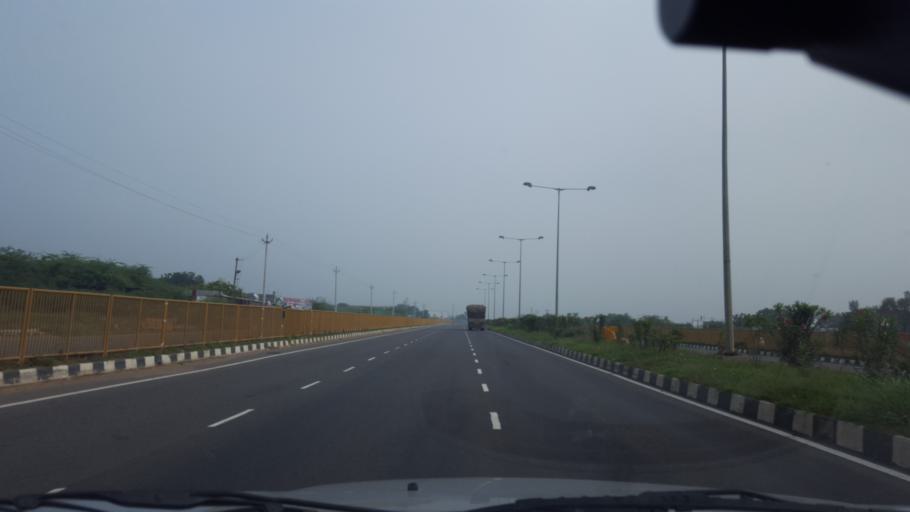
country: IN
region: Andhra Pradesh
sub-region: Guntur
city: Chilakalurupet
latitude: 16.0030
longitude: 80.1126
